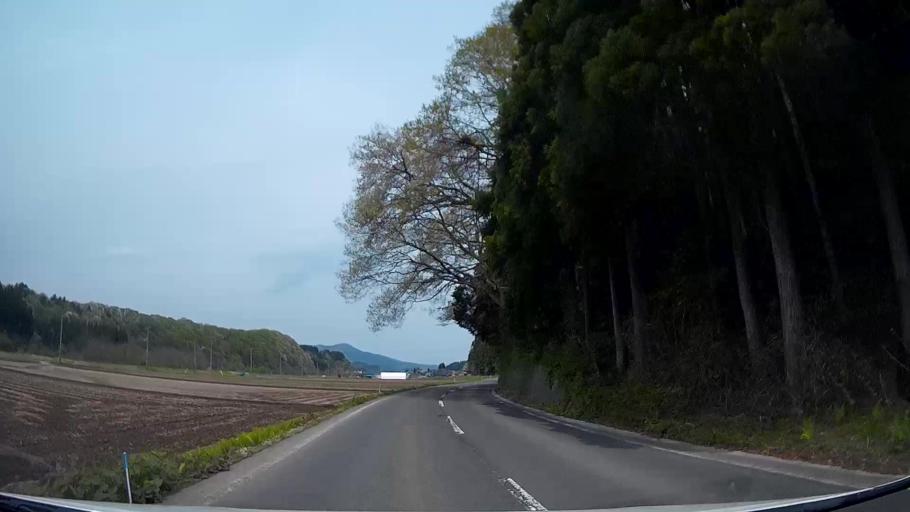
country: JP
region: Akita
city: Hanawa
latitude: 40.0811
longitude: 140.7907
